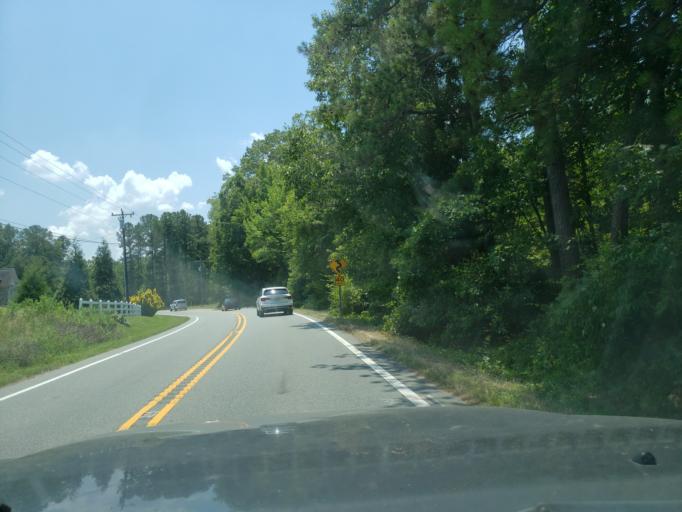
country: US
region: North Carolina
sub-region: Wake County
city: Green Level
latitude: 35.8640
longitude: -78.9438
